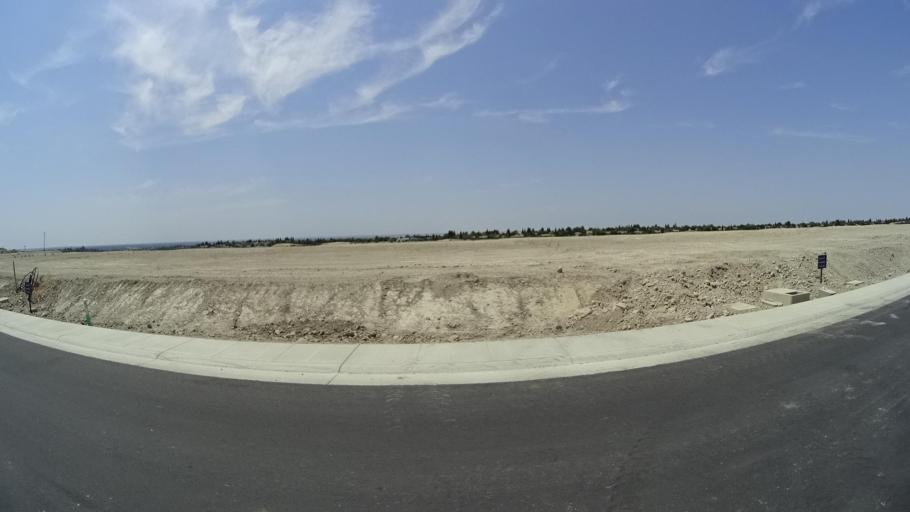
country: US
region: California
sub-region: Placer County
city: Rocklin
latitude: 38.8144
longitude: -121.2294
